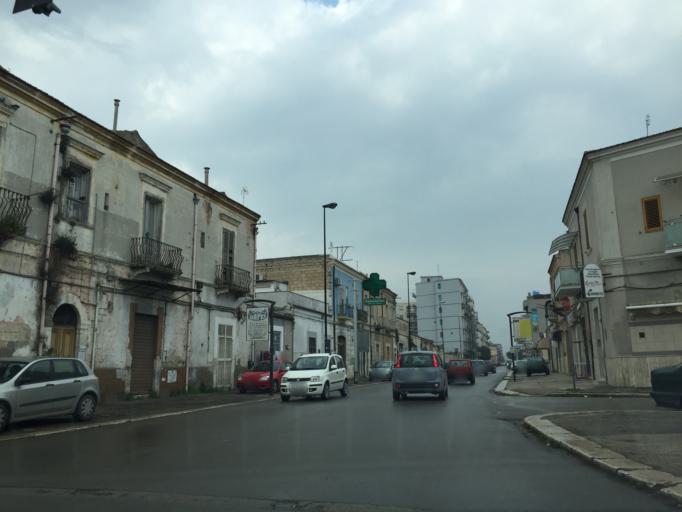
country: IT
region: Apulia
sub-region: Provincia di Foggia
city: Foggia
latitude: 41.4651
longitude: 15.5399
